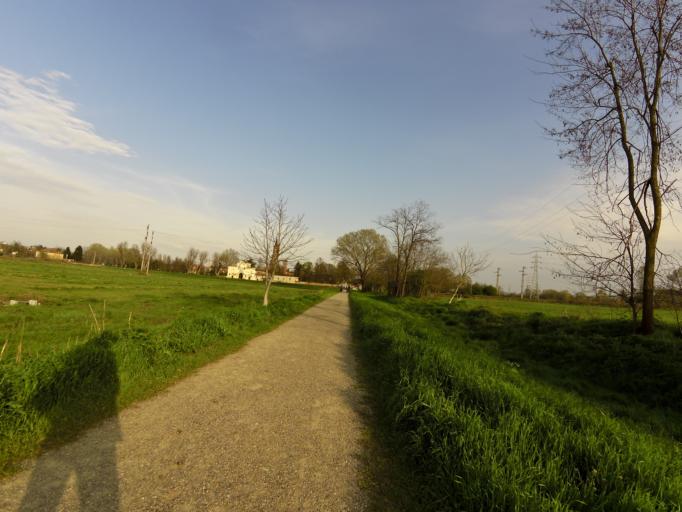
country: IT
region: Lombardy
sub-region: Citta metropolitana di Milano
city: Chiaravalle
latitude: 45.4170
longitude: 9.2323
